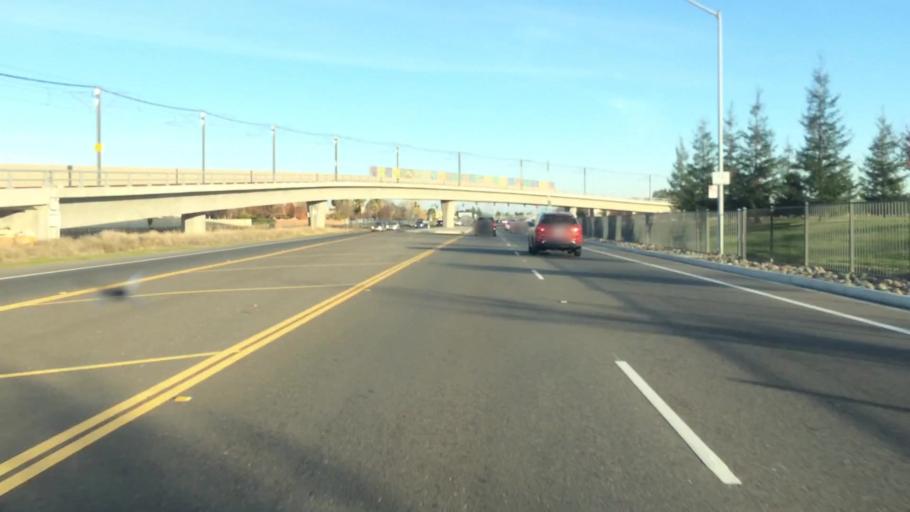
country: US
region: California
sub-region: Sacramento County
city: Laguna
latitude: 38.4579
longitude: -121.4211
